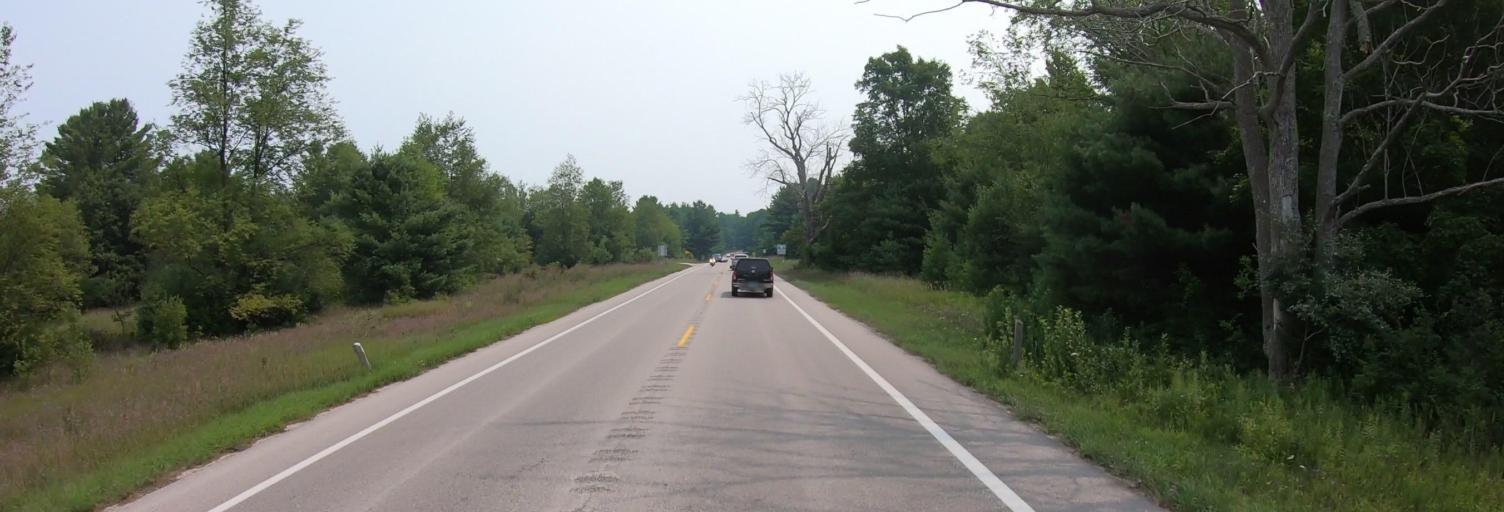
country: US
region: Michigan
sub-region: Leelanau County
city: Leland
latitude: 44.9334
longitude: -85.8980
